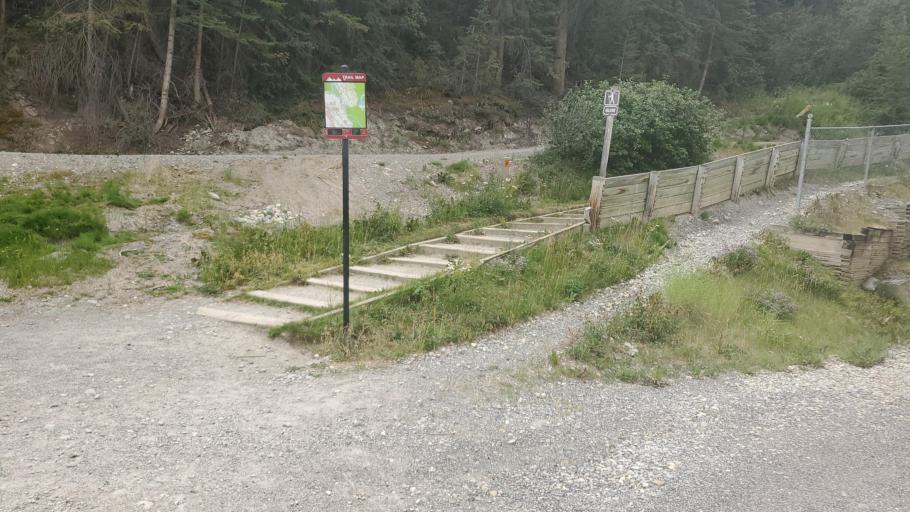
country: CA
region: Alberta
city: Canmore
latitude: 51.0886
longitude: -115.3732
